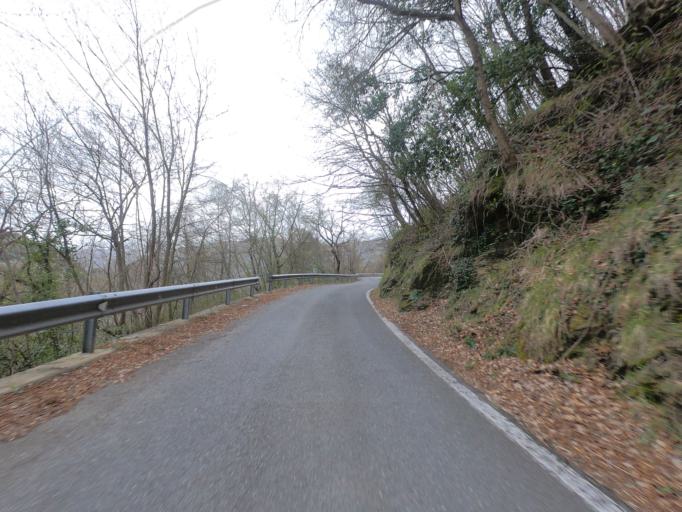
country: IT
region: Liguria
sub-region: Provincia di Savona
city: Testico
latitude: 44.0311
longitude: 8.0145
